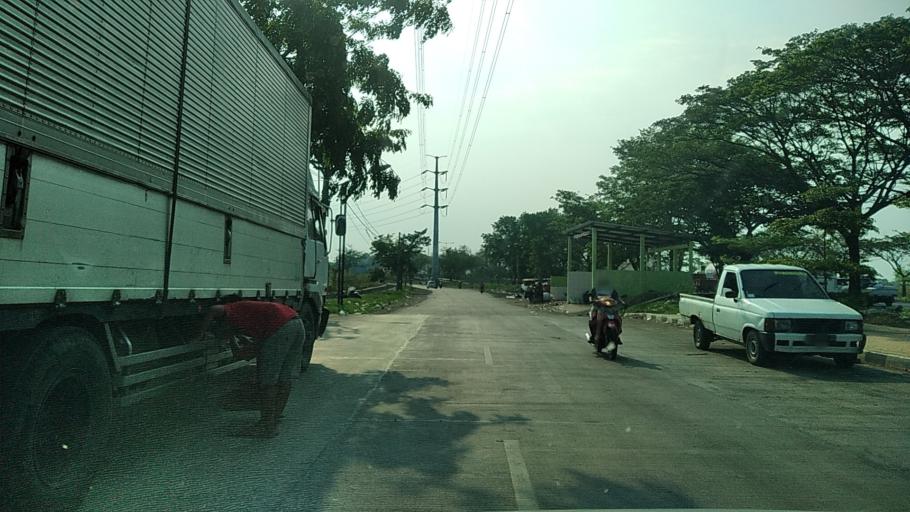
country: ID
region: Central Java
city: Semarang
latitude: -6.9544
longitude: 110.4017
